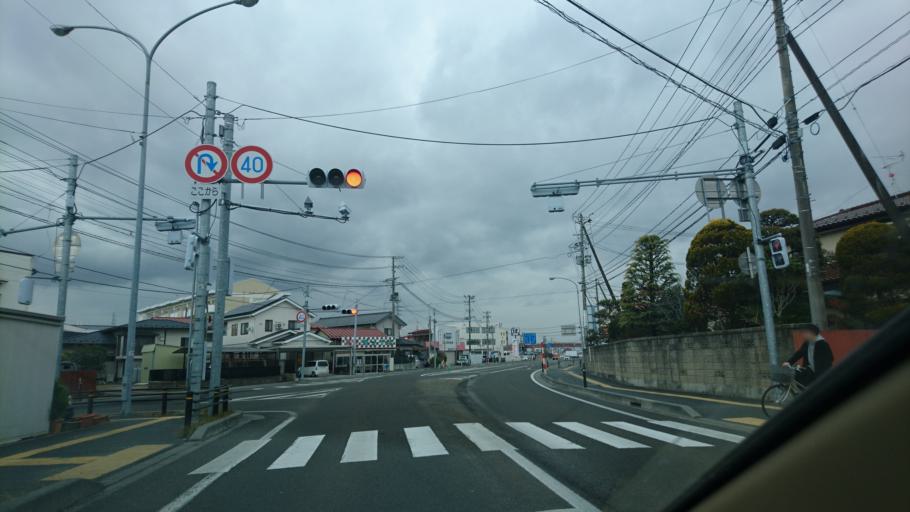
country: JP
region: Miyagi
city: Furukawa
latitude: 38.5833
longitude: 140.9506
